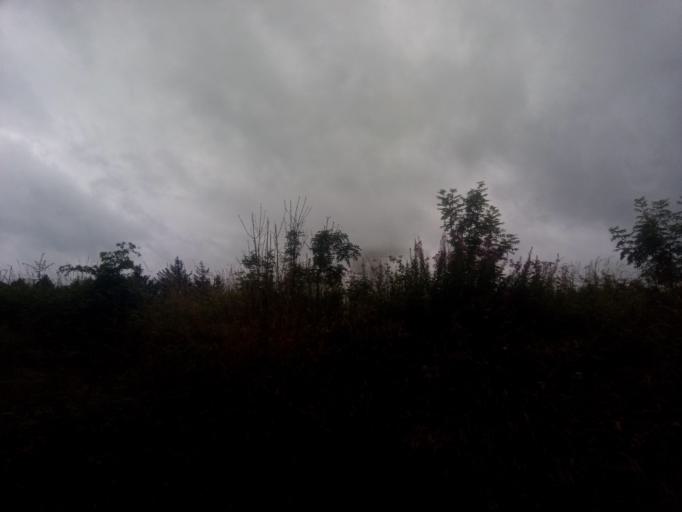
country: GB
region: England
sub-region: North Yorkshire
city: Settle
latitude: 54.0184
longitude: -2.2582
